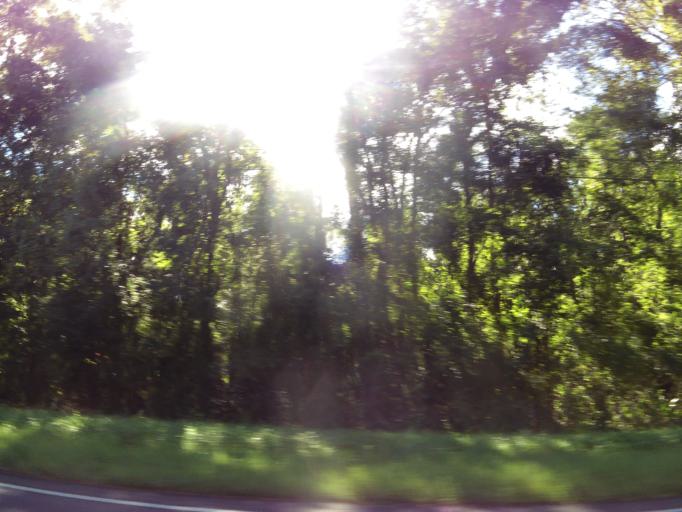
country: US
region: Georgia
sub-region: Camden County
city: Woodbine
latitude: 31.0450
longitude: -81.7297
